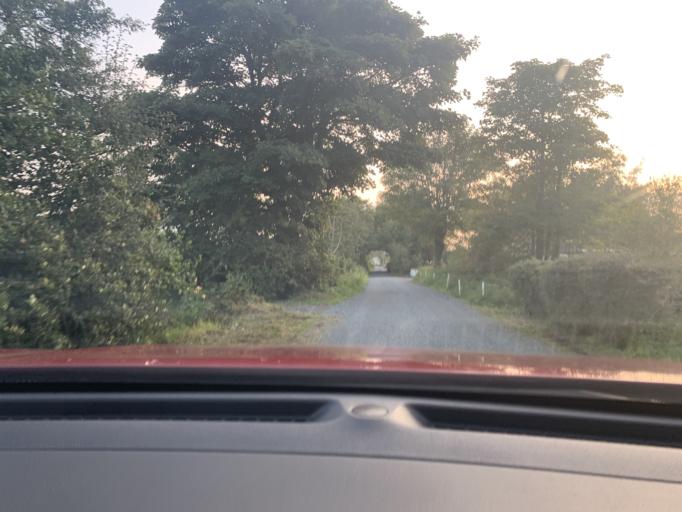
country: IE
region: Connaught
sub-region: County Leitrim
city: Kinlough
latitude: 54.4340
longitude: -8.4370
